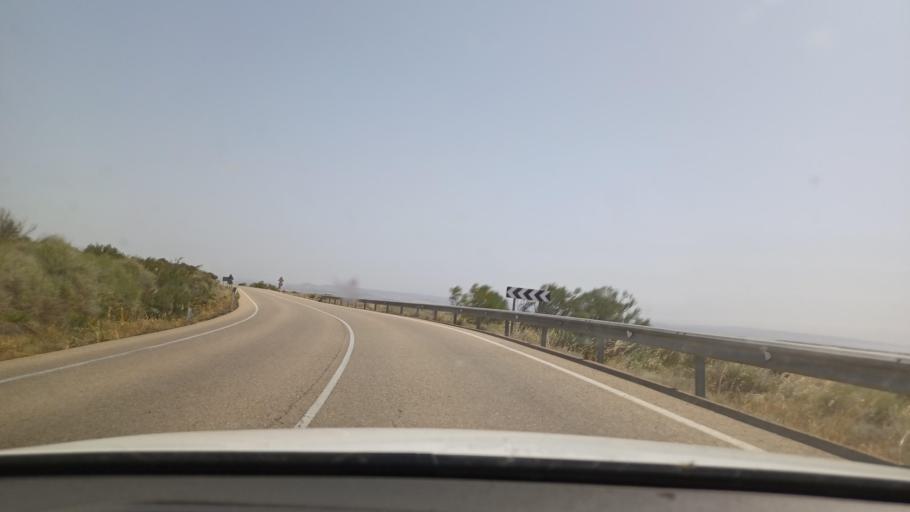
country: ES
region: Aragon
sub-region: Provincia de Zaragoza
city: Chiprana
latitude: 41.3329
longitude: -0.0893
